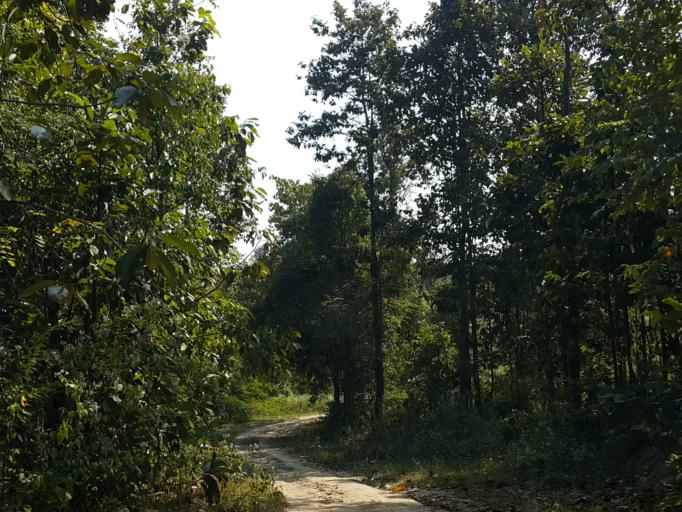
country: TH
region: Chiang Mai
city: Hot
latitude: 18.1245
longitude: 98.4395
